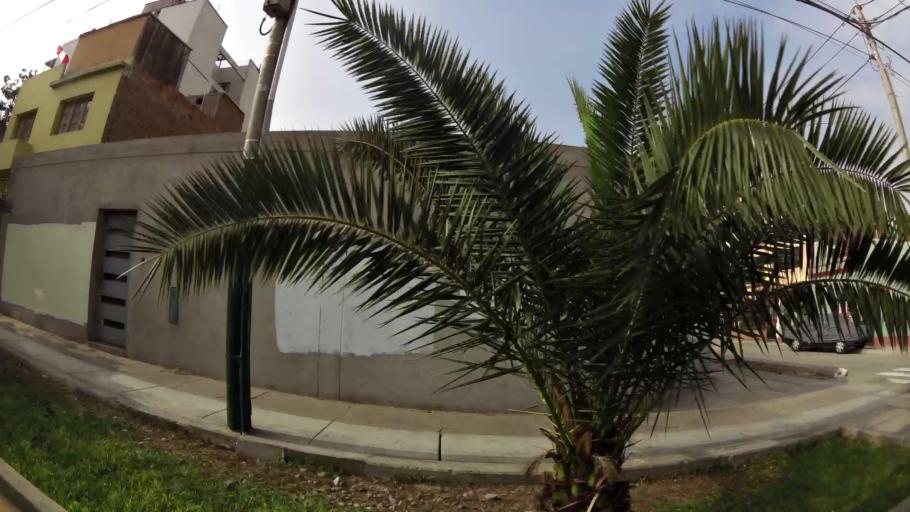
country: PE
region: Lima
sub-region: Lima
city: San Isidro
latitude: -12.0939
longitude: -77.0655
